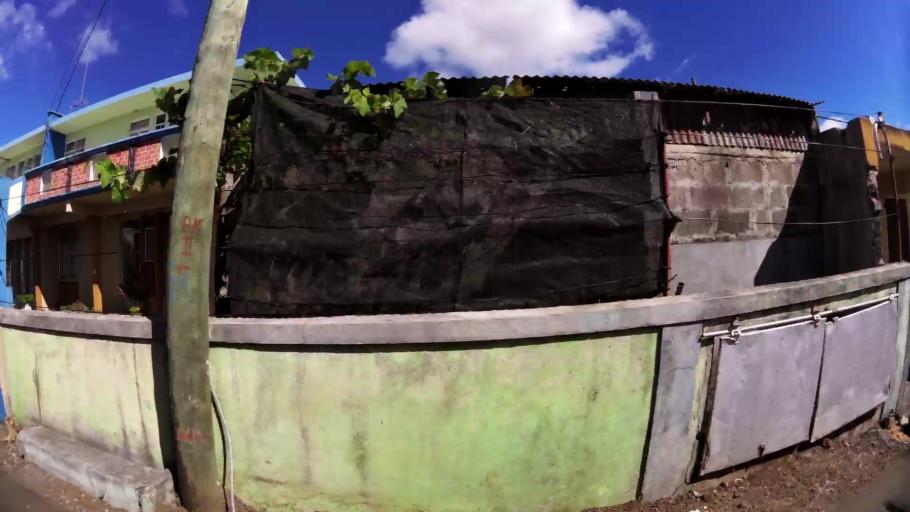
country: MU
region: Plaines Wilhems
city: Vacoas
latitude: -20.2938
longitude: 57.4815
